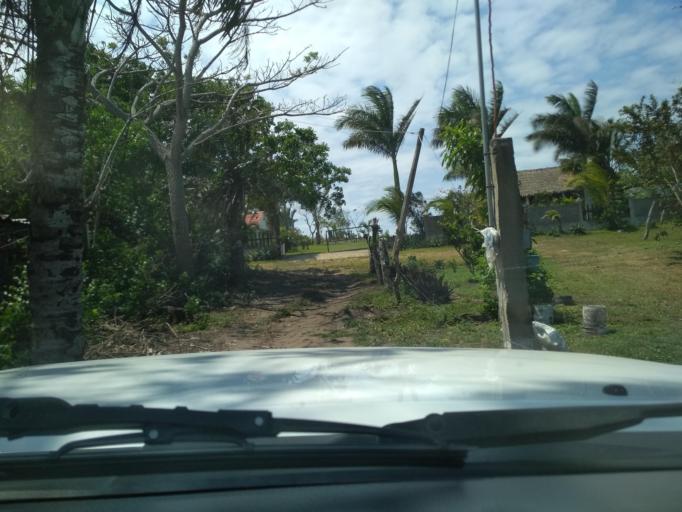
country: MX
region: Veracruz
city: Anton Lizardo
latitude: 19.0077
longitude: -95.9931
